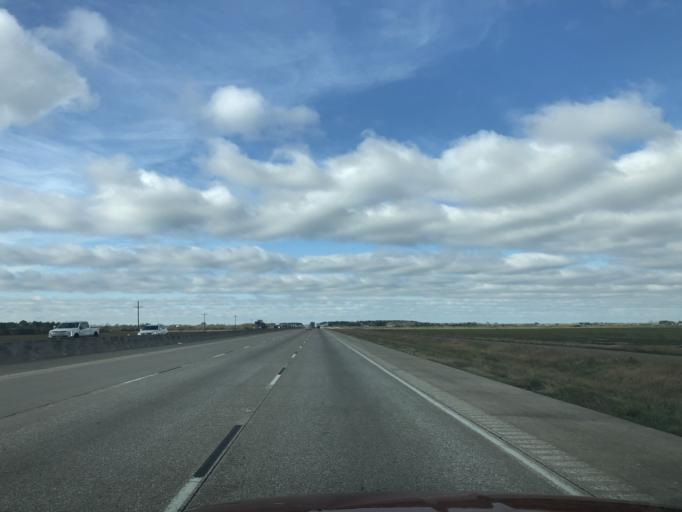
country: US
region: Texas
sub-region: Chambers County
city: Anahuac
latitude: 29.8359
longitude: -94.5576
